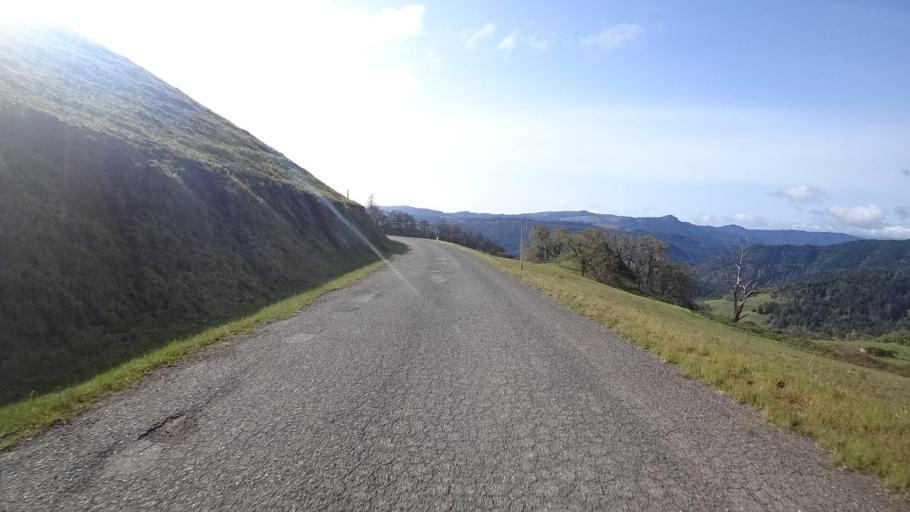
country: US
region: California
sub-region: Humboldt County
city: Hydesville
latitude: 40.6396
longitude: -123.9022
